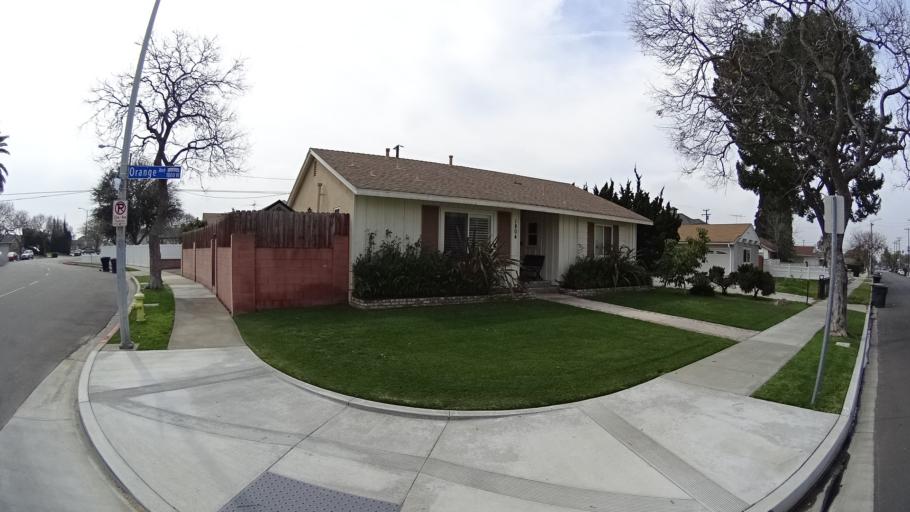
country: US
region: California
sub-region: Orange County
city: Anaheim
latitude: 33.8251
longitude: -117.9463
